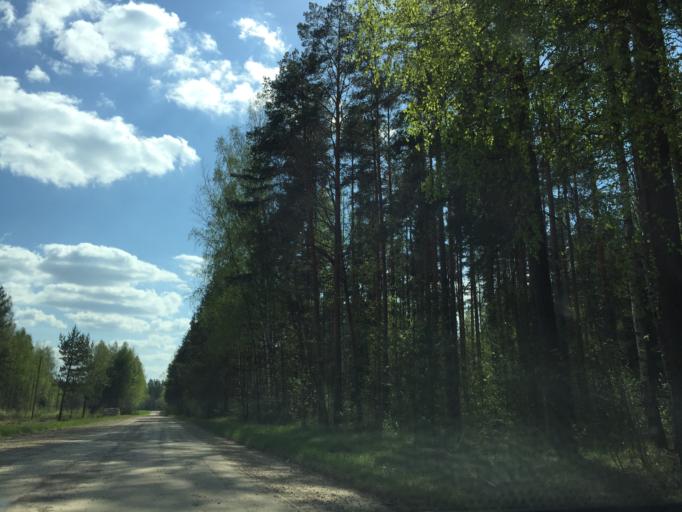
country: LV
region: Vecumnieki
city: Vecumnieki
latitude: 56.4809
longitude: 24.5342
